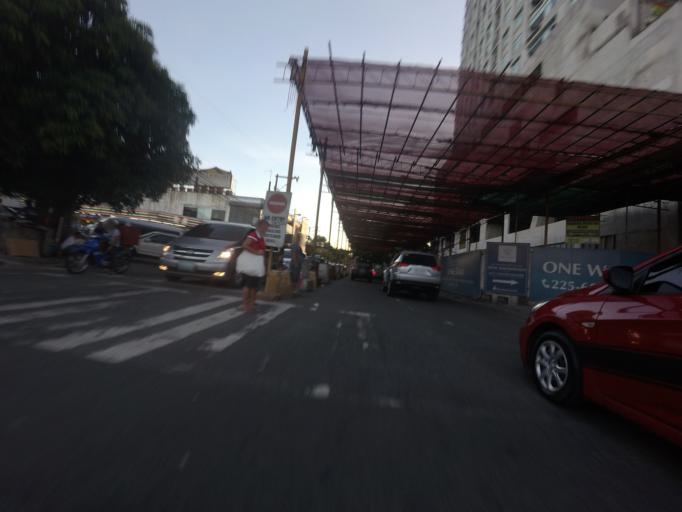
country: PH
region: Metro Manila
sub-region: San Juan
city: San Juan
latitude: 14.6008
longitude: 121.0477
